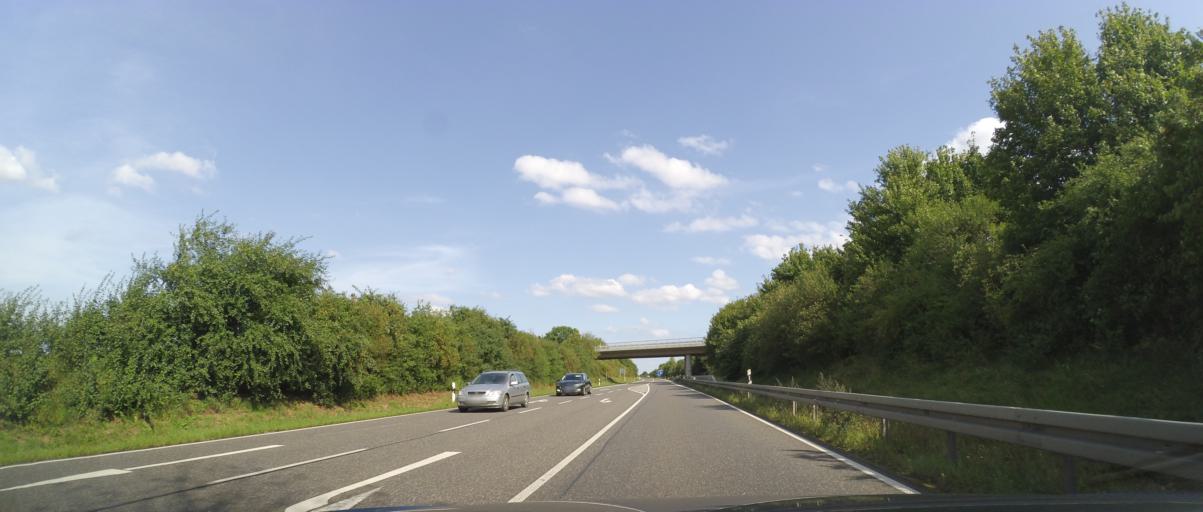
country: DE
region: North Rhine-Westphalia
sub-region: Regierungsbezirk Koln
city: Euskirchen
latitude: 50.6783
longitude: 6.7312
